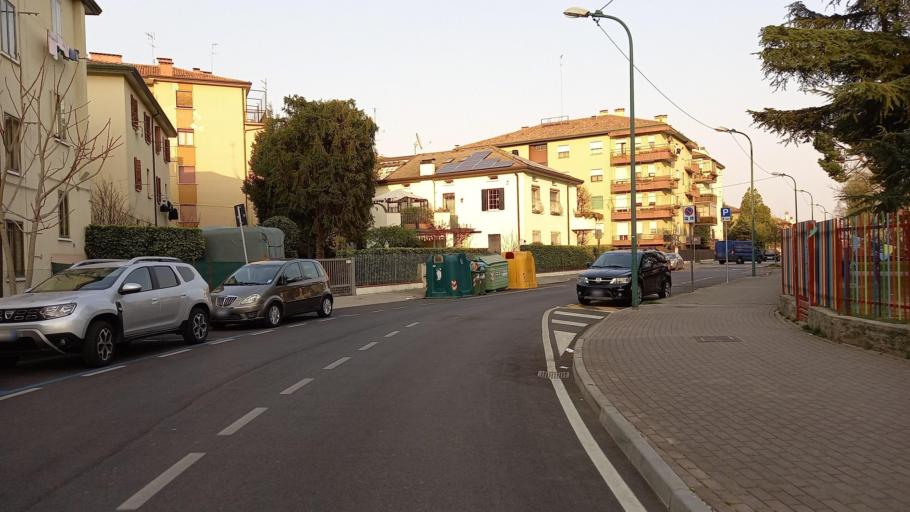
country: IT
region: Veneto
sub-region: Provincia di Venezia
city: Mestre
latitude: 45.4905
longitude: 12.2276
